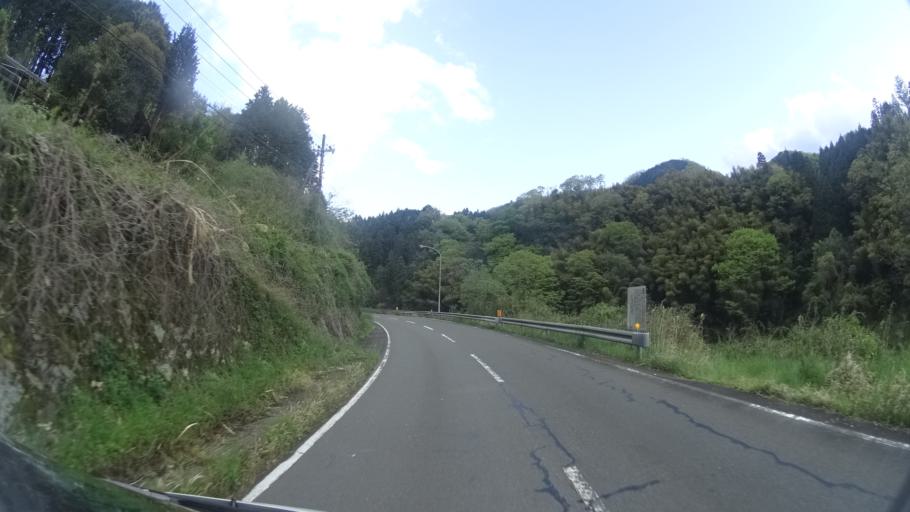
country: JP
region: Kyoto
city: Ayabe
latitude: 35.2711
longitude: 135.3659
